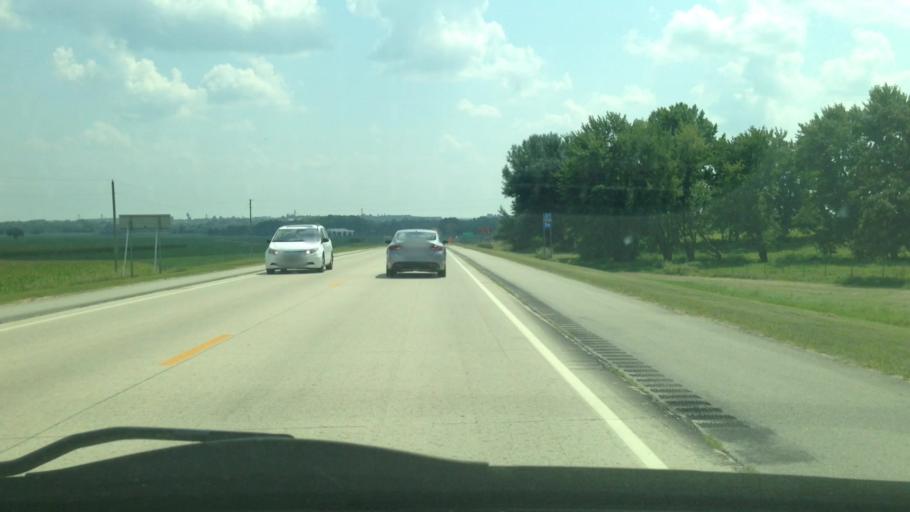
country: US
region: Minnesota
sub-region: Fillmore County
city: Spring Valley
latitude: 43.5121
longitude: -92.3694
